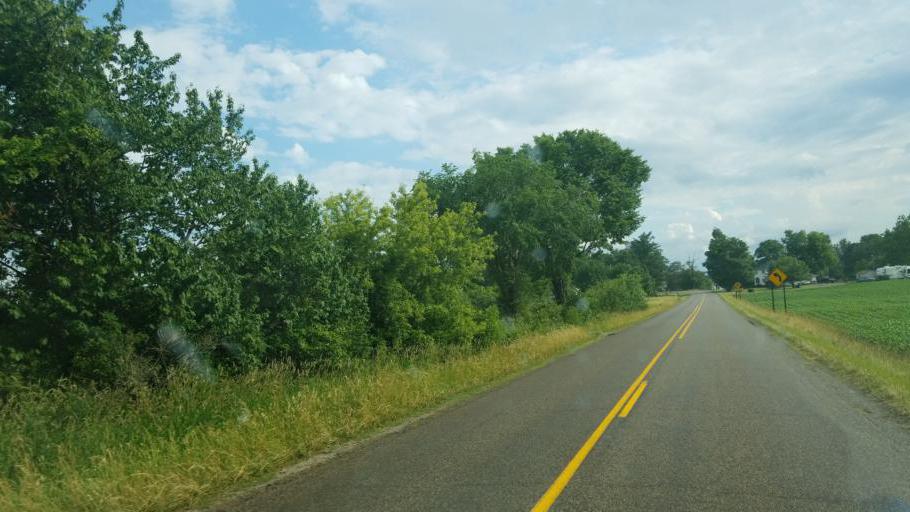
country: US
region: Michigan
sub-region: Eaton County
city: Bellevue
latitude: 42.4972
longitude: -85.0212
